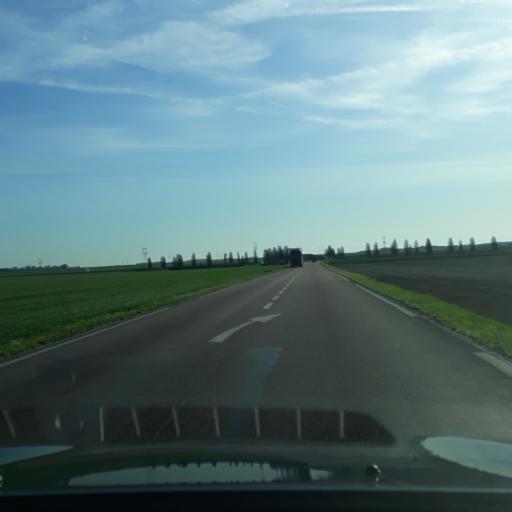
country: FR
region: Ile-de-France
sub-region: Departement de l'Essonne
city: Corbreuse
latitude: 48.4505
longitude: 1.9975
